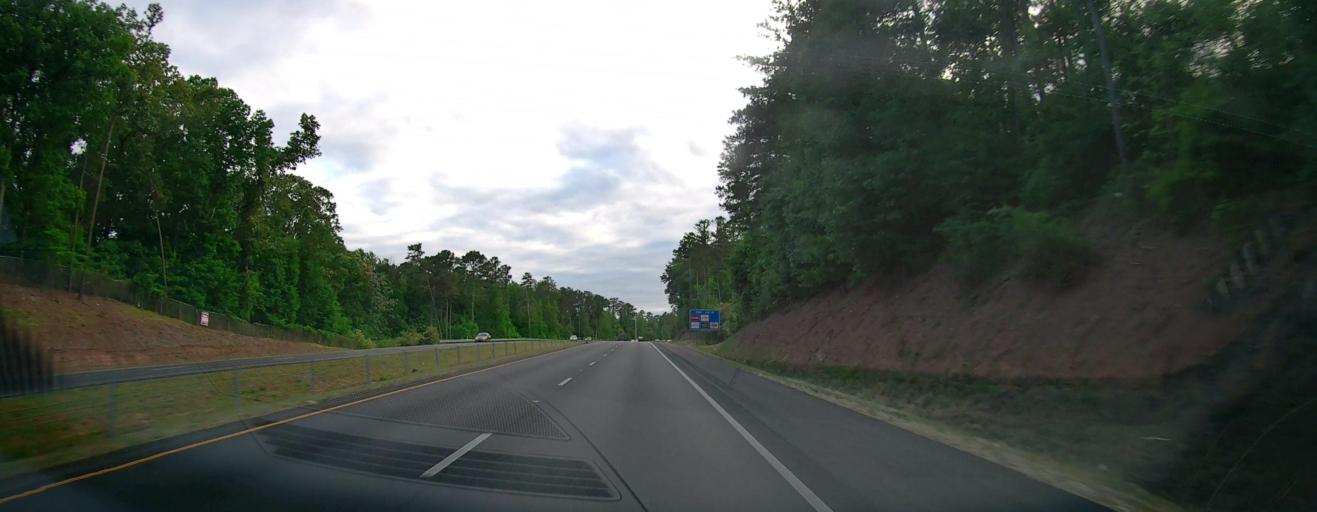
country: US
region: Georgia
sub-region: Clarke County
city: Country Club Estates
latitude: 33.9522
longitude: -83.4418
